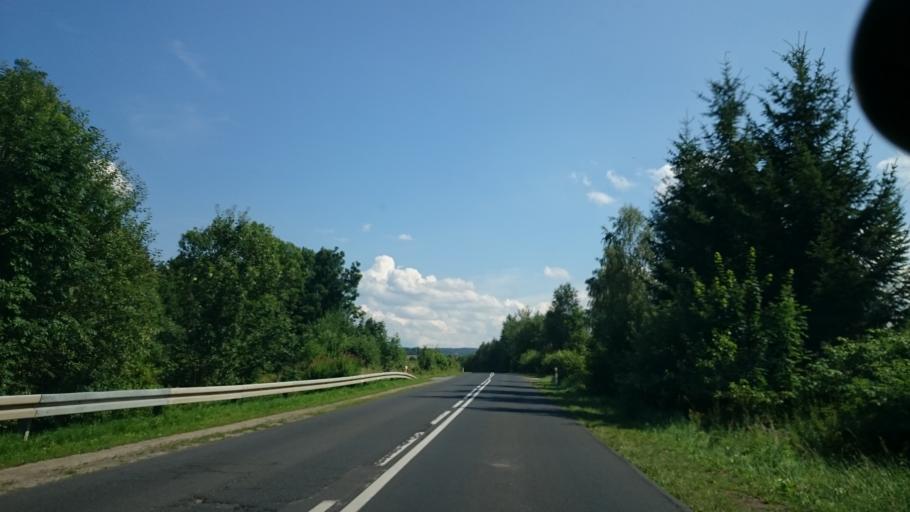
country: PL
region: Lower Silesian Voivodeship
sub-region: Powiat klodzki
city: Ladek-Zdroj
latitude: 50.3421
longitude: 16.8011
